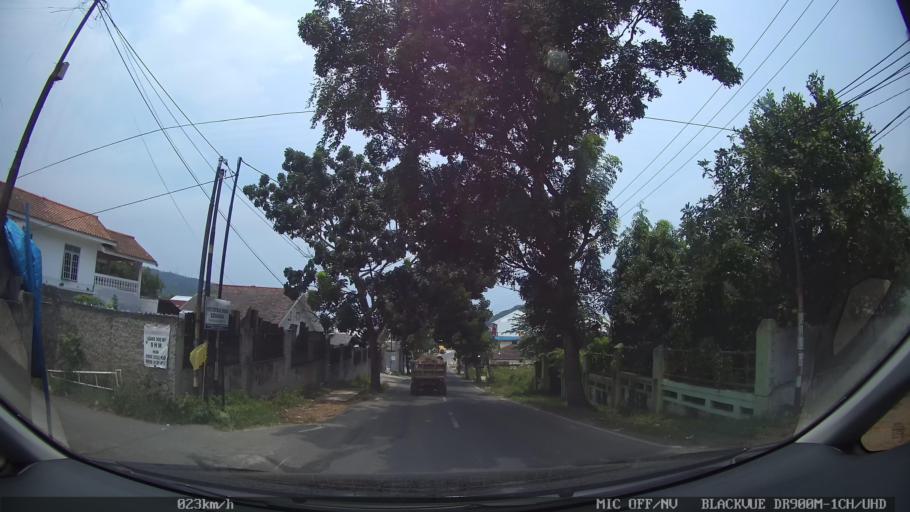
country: ID
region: Lampung
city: Bandarlampung
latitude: -5.4091
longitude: 105.2888
